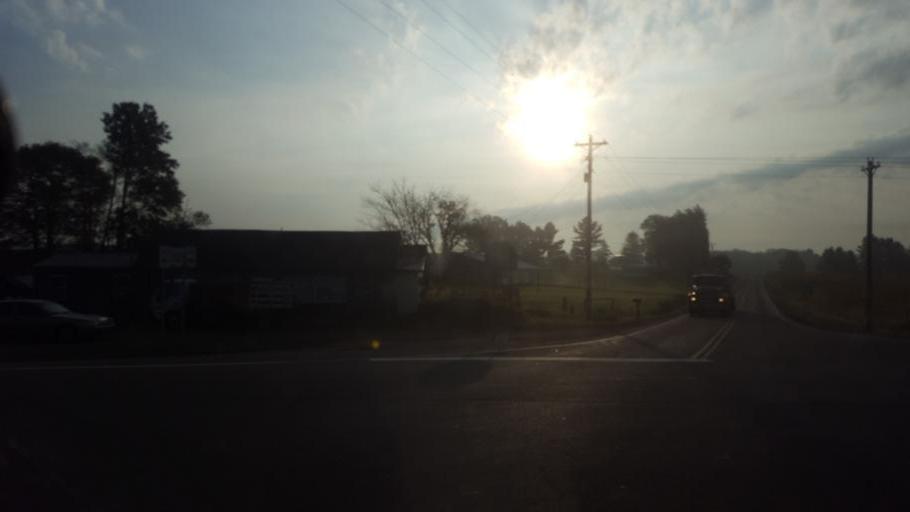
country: US
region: Ohio
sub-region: Knox County
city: Oak Hill
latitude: 40.3461
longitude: -82.3015
